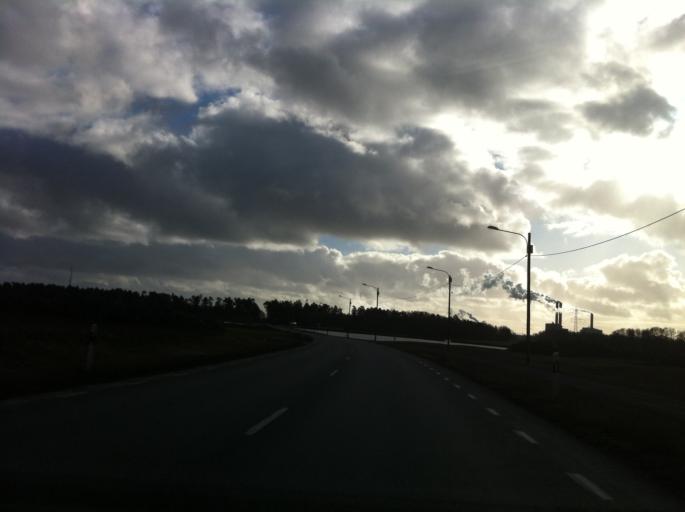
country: SE
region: Blekinge
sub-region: Solvesborgs Kommun
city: Soelvesborg
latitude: 56.0632
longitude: 14.5477
